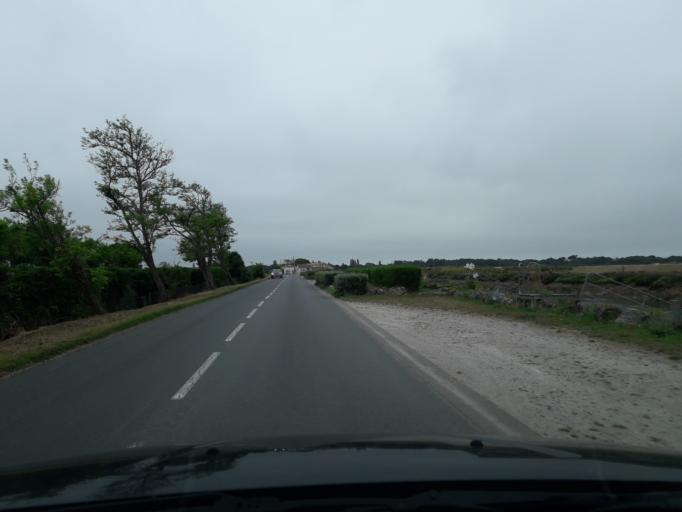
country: FR
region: Poitou-Charentes
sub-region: Departement de la Charente-Maritime
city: Boyard-Ville
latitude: 45.9622
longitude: -1.2472
